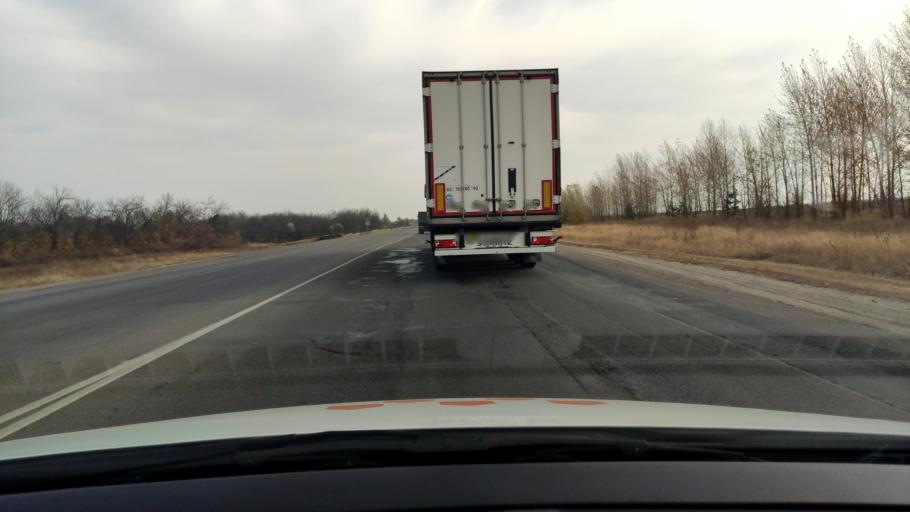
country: RU
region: Voronezj
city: Somovo
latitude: 51.6978
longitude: 39.3991
